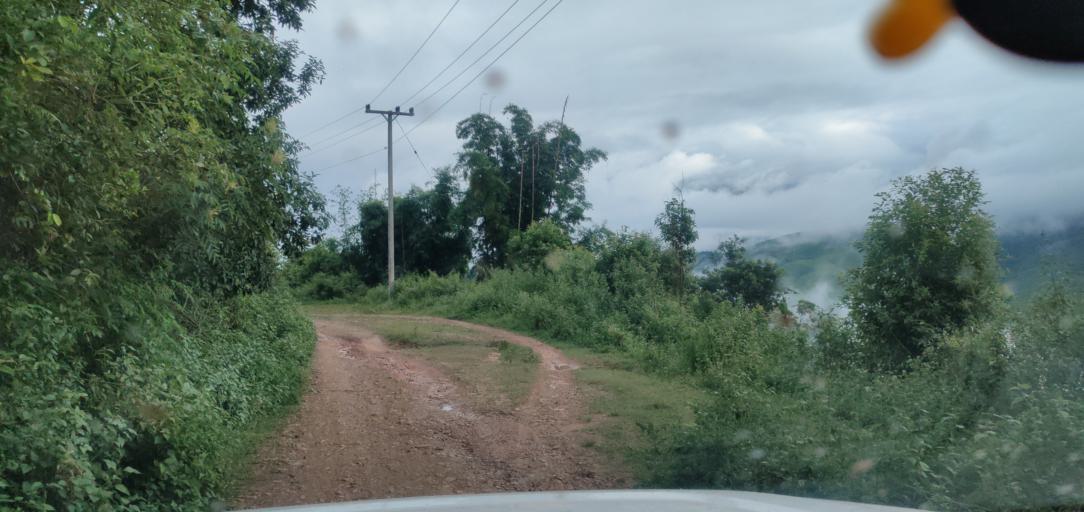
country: LA
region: Phongsali
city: Phongsali
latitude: 21.4442
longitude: 102.2934
